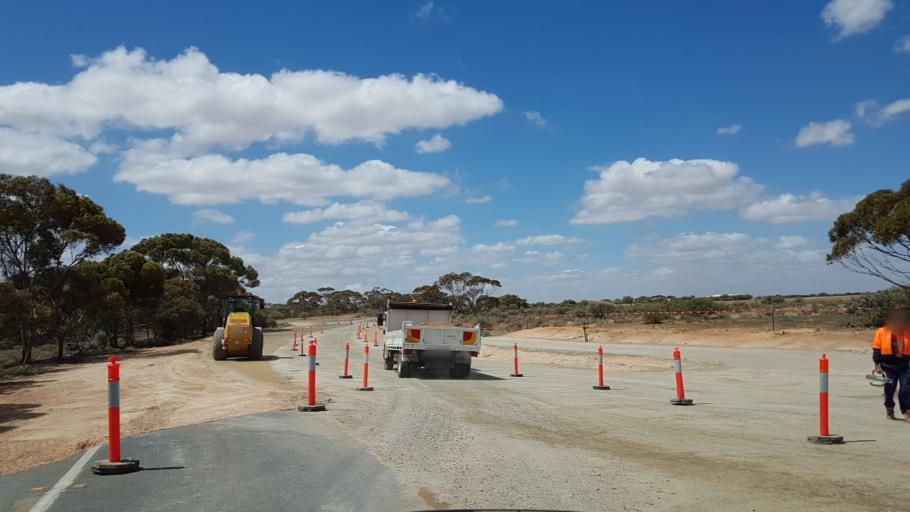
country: AU
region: South Australia
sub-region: Loxton Waikerie
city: Waikerie
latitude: -34.1880
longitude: 140.0173
